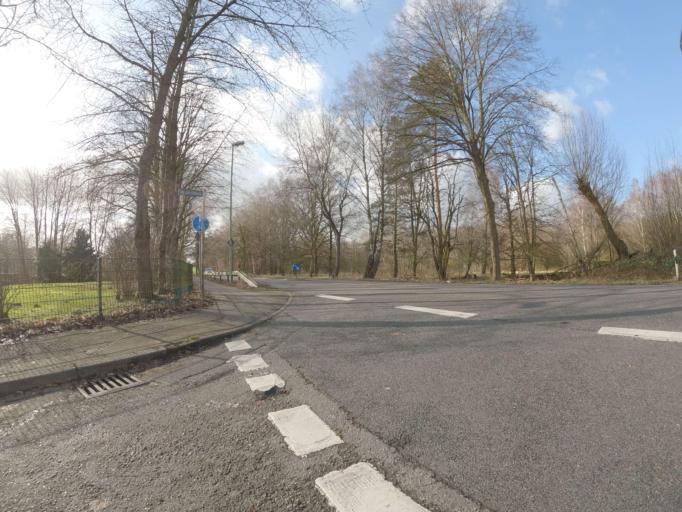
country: DE
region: North Rhine-Westphalia
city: Stolberg
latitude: 50.7795
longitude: 6.1964
